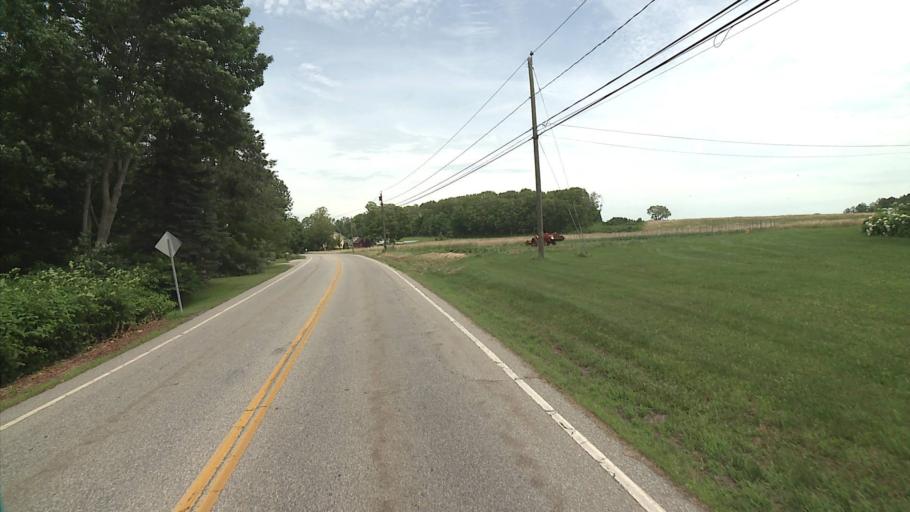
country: US
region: Connecticut
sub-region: New London County
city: Preston City
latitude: 41.5334
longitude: -71.9704
